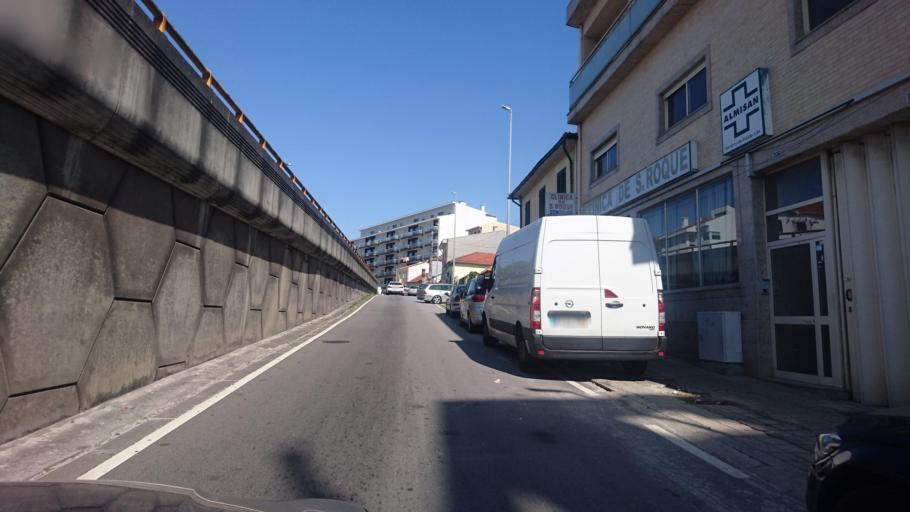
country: PT
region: Porto
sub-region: Gondomar
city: Rio Tinto
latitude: 41.1672
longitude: -8.5672
